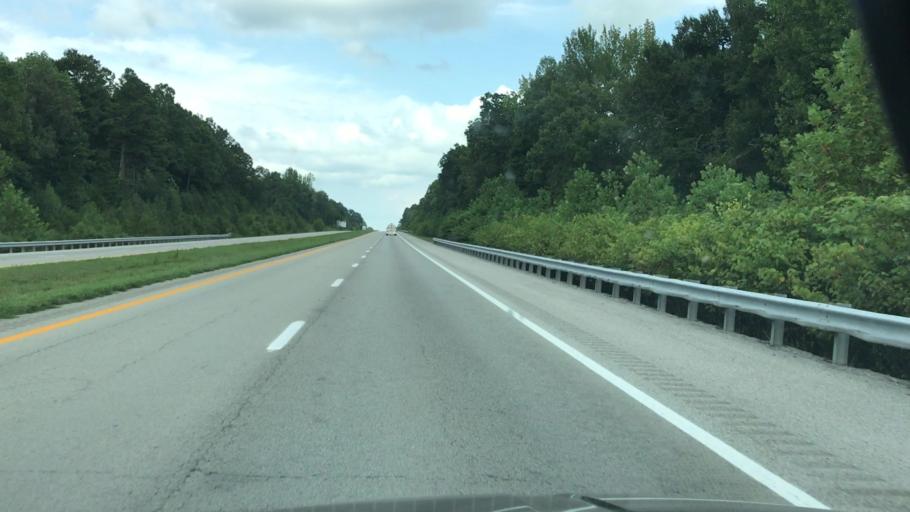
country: US
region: Kentucky
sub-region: Hopkins County
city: Dawson Springs
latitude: 37.1975
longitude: -87.6520
